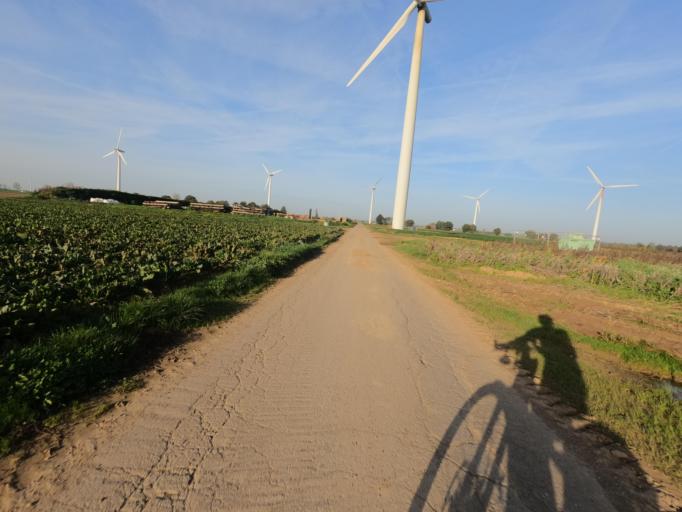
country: DE
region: North Rhine-Westphalia
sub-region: Regierungsbezirk Koln
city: Titz
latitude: 51.0632
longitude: 6.4133
